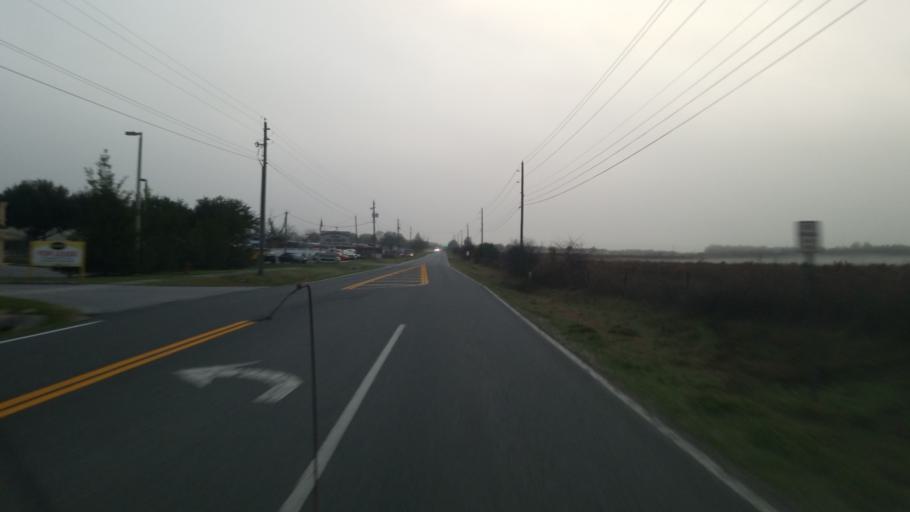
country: US
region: Florida
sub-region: Marion County
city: Ocala
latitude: 29.1501
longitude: -82.2260
